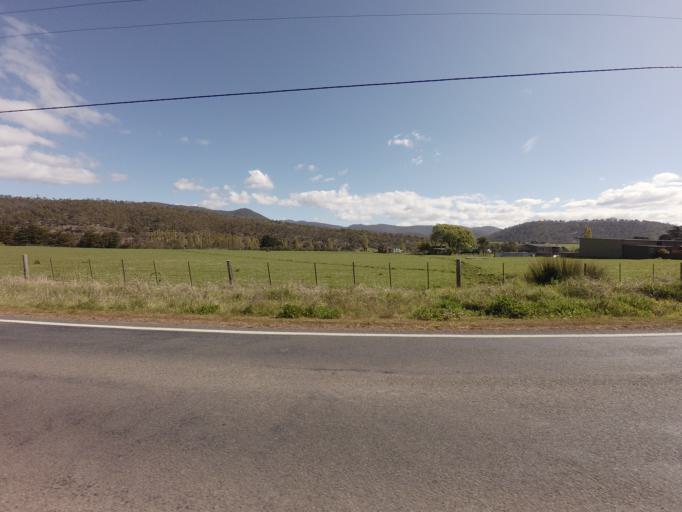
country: AU
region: Tasmania
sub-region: Derwent Valley
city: New Norfolk
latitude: -42.7738
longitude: 147.0350
